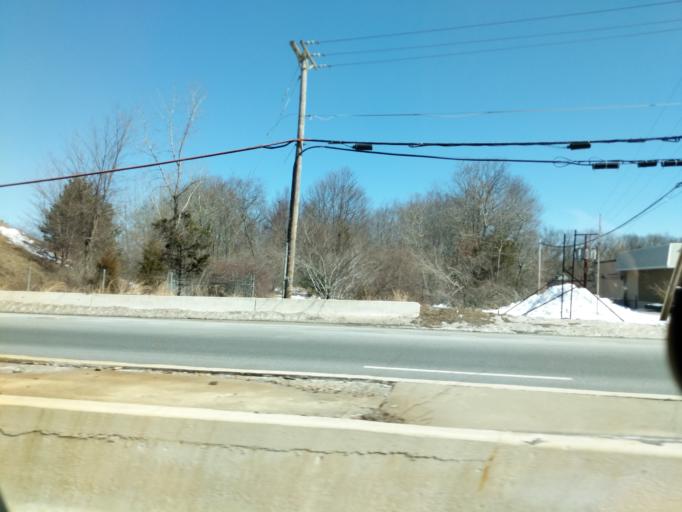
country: US
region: Rhode Island
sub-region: Providence County
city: Cumberland Hill
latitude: 41.9507
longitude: -71.4850
